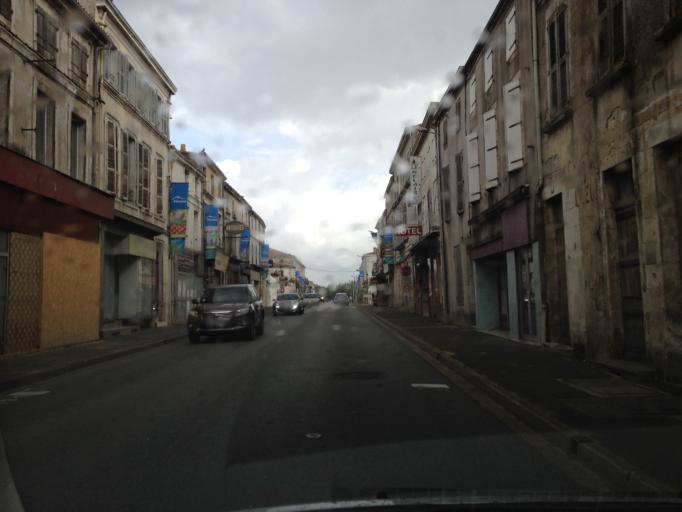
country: FR
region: Poitou-Charentes
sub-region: Departement de la Charente-Maritime
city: Marans
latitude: 46.3105
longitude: -0.9918
